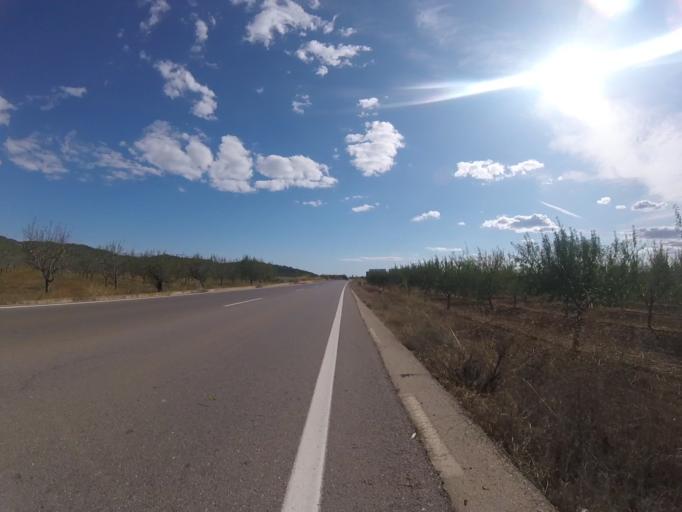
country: ES
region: Valencia
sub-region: Provincia de Castello
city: Alcala de Xivert
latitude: 40.2622
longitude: 0.2432
